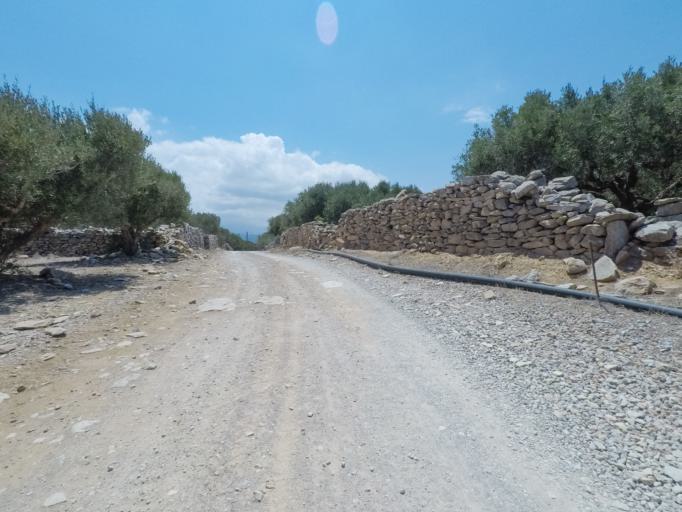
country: GR
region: Crete
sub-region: Nomos Lasithiou
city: Elounda
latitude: 35.3207
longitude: 25.7510
